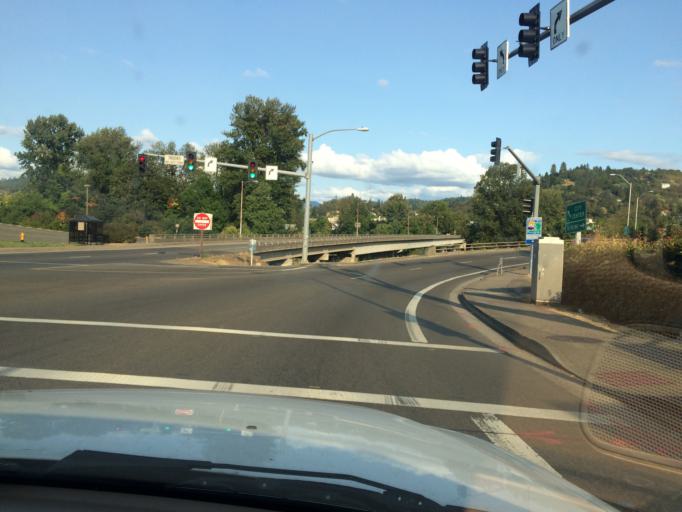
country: US
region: Oregon
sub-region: Douglas County
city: Roseburg
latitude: 43.2127
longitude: -123.3520
